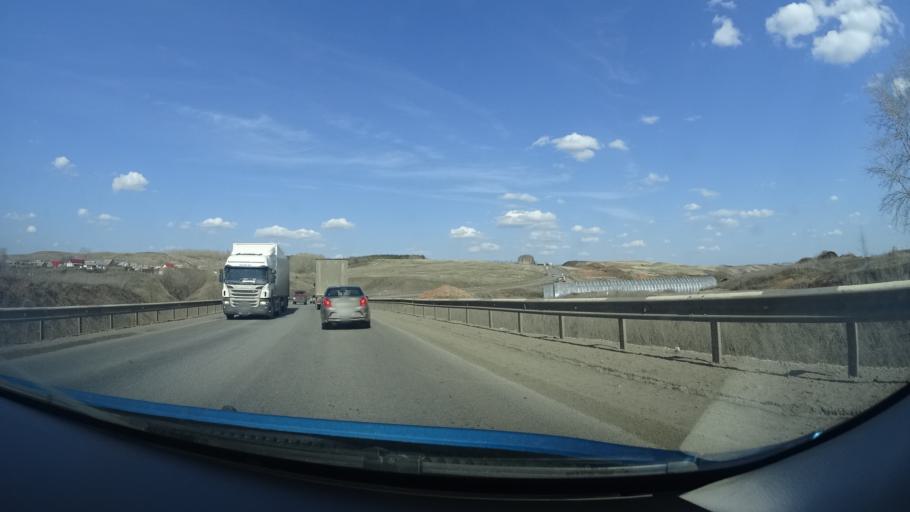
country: RU
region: Bashkortostan
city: Buzdyak
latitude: 54.6297
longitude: 54.4632
